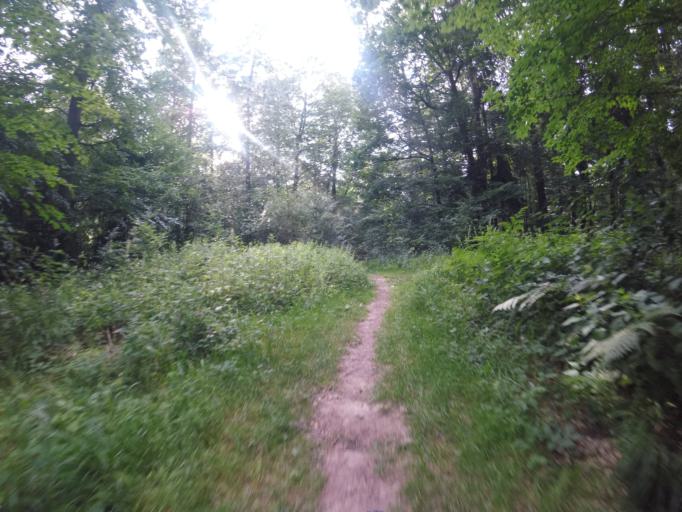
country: DE
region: Baden-Wuerttemberg
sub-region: Regierungsbezirk Stuttgart
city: Sulzbach an der Murr
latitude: 48.9732
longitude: 9.4981
